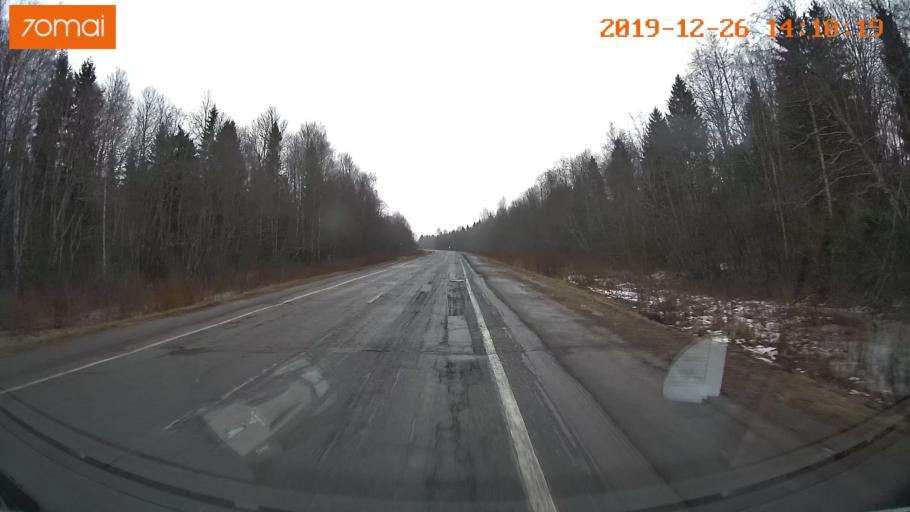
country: RU
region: Jaroslavl
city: Poshekhon'ye
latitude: 58.5083
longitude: 38.9506
